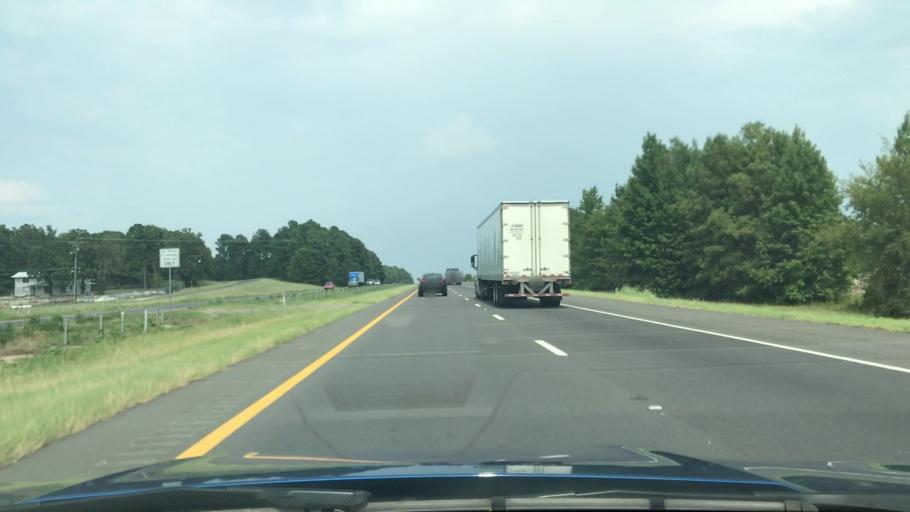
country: US
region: Texas
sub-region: Harrison County
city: Hallsville
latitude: 32.4637
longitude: -94.6415
